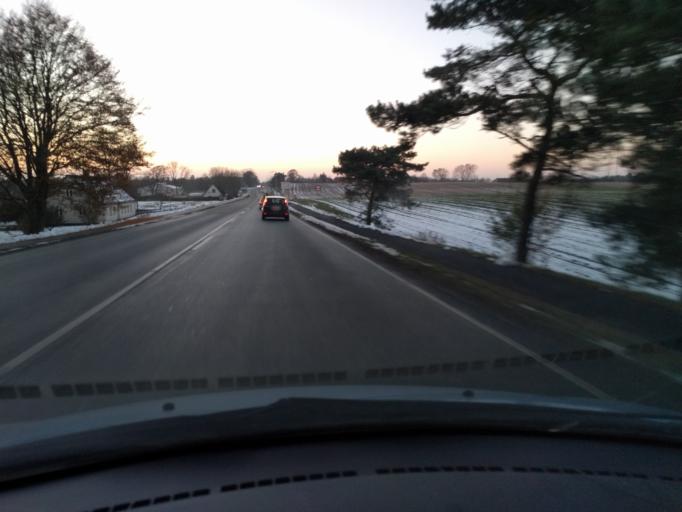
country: DK
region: South Denmark
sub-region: Nyborg Kommune
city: Ullerslev
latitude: 55.3609
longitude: 10.6849
